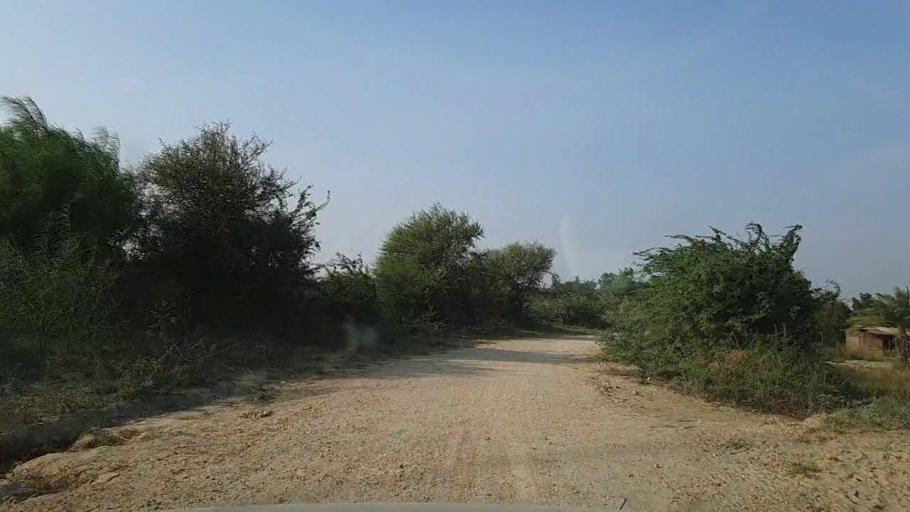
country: PK
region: Sindh
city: Mirpur Sakro
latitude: 24.5890
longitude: 67.6496
